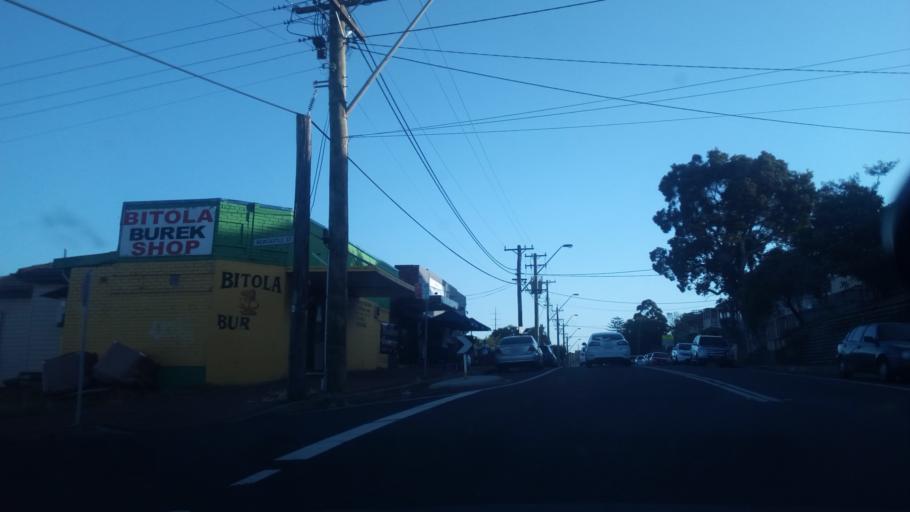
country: AU
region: New South Wales
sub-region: Wollongong
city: Cringila
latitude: -34.4696
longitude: 150.8718
